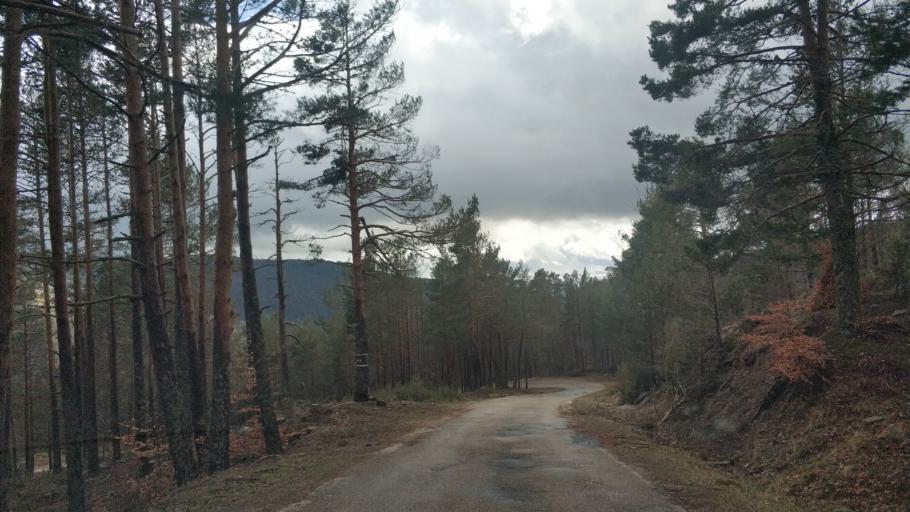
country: ES
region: Castille and Leon
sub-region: Provincia de Burgos
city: Neila
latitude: 42.0451
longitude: -3.0186
